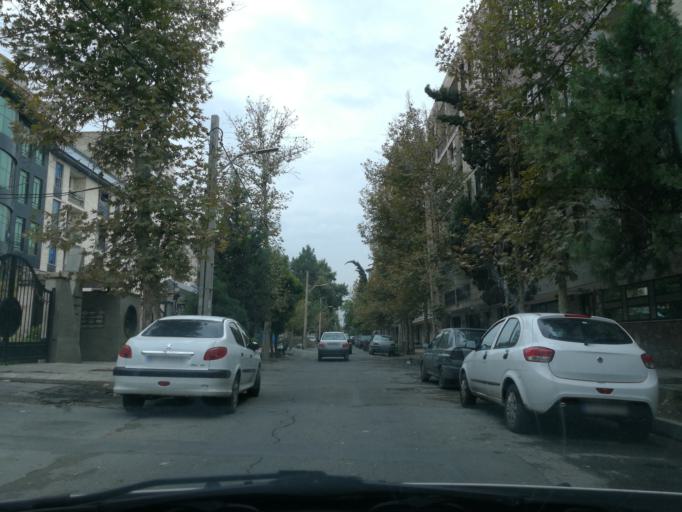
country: IR
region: Alborz
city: Karaj
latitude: 35.8548
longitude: 50.9536
